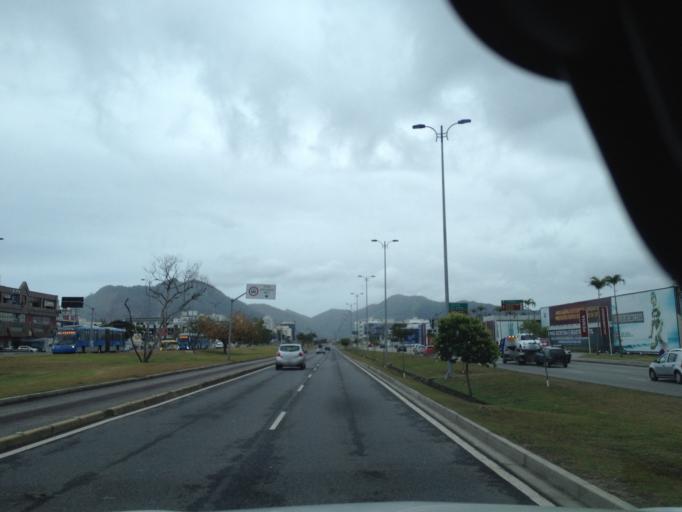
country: BR
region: Rio de Janeiro
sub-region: Nilopolis
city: Nilopolis
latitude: -23.0155
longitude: -43.4714
